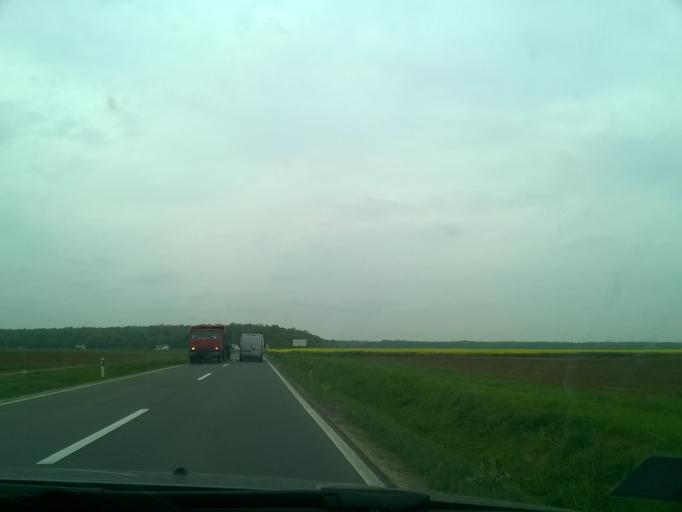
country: RS
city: Hrtkovci
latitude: 44.8470
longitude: 19.7684
